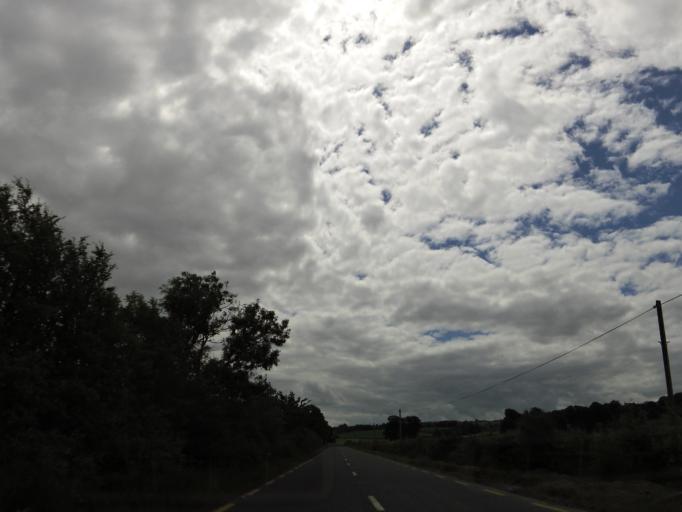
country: IE
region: Munster
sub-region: North Tipperary
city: Nenagh
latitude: 52.7768
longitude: -8.0296
